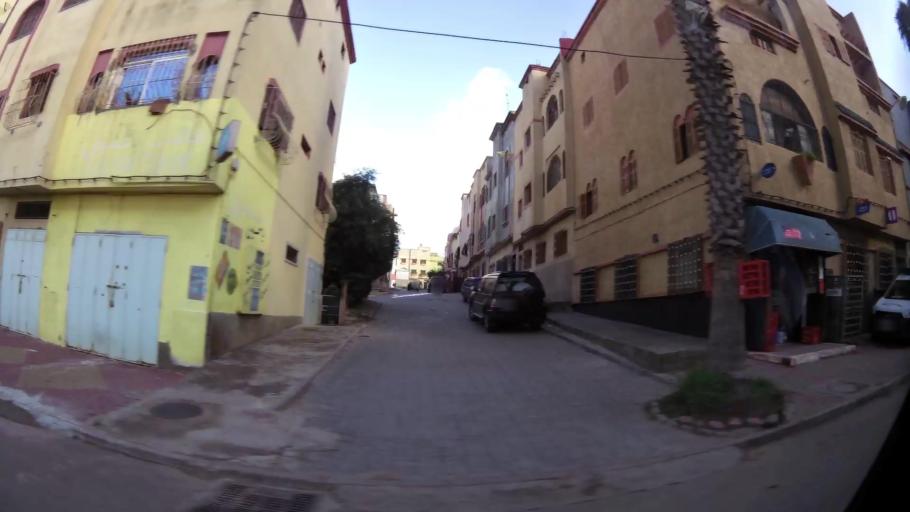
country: MA
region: Chaouia-Ouardigha
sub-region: Settat Province
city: Settat
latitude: 33.0059
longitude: -7.6336
